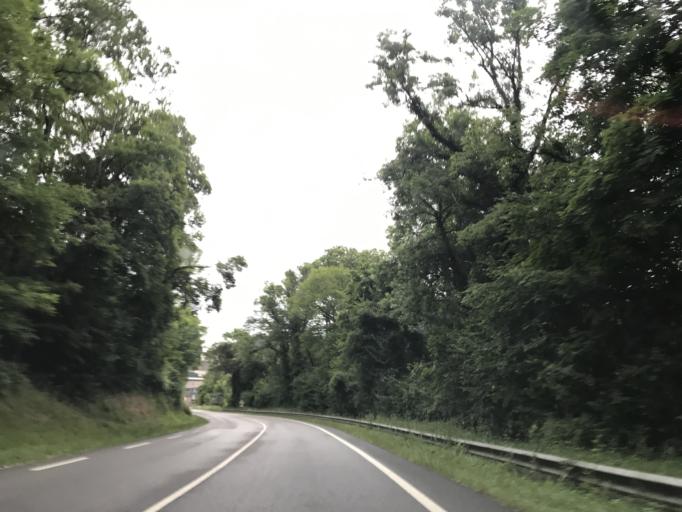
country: FR
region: Ile-de-France
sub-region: Departement des Yvelines
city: Bennecourt
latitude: 49.0313
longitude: 1.5581
